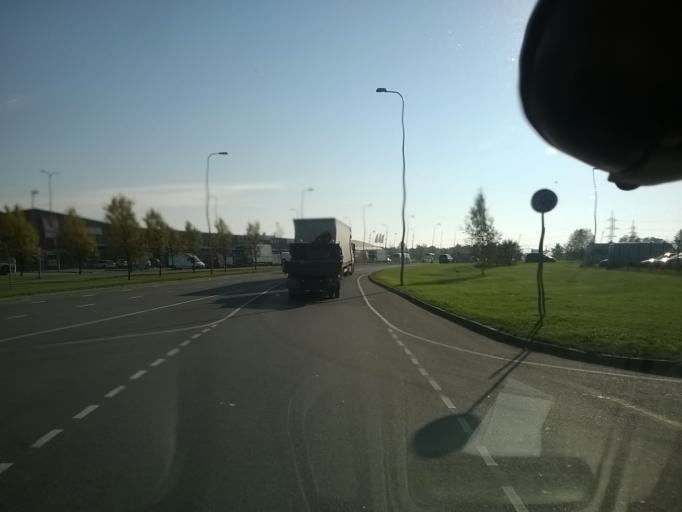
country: EE
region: Harju
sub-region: Tallinna linn
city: Kose
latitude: 59.4281
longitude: 24.8364
